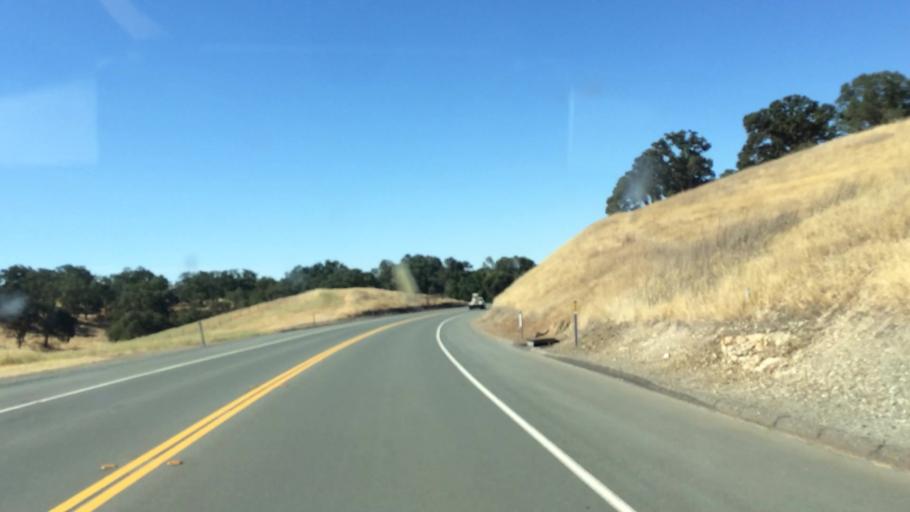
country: US
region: California
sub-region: Amador County
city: Plymouth
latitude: 38.4466
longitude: -120.8724
